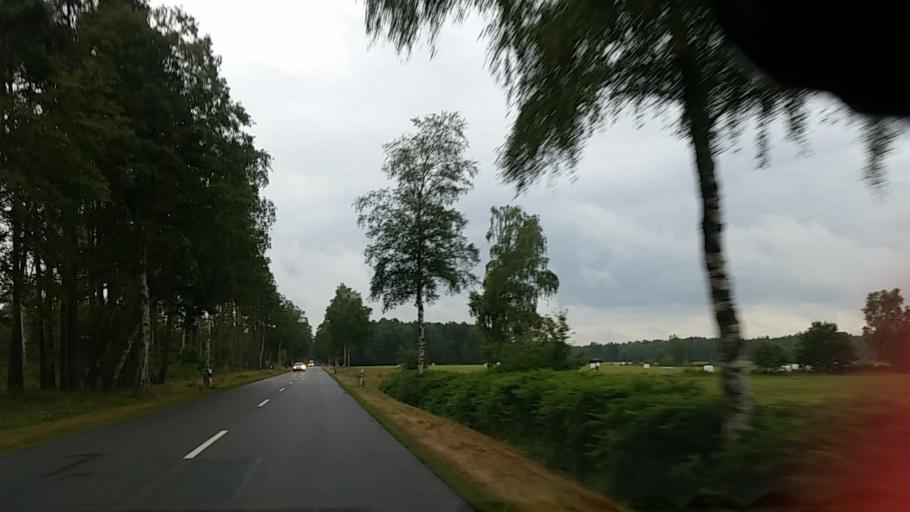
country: DE
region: Lower Saxony
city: Schoneworde
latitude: 52.6551
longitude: 10.6988
